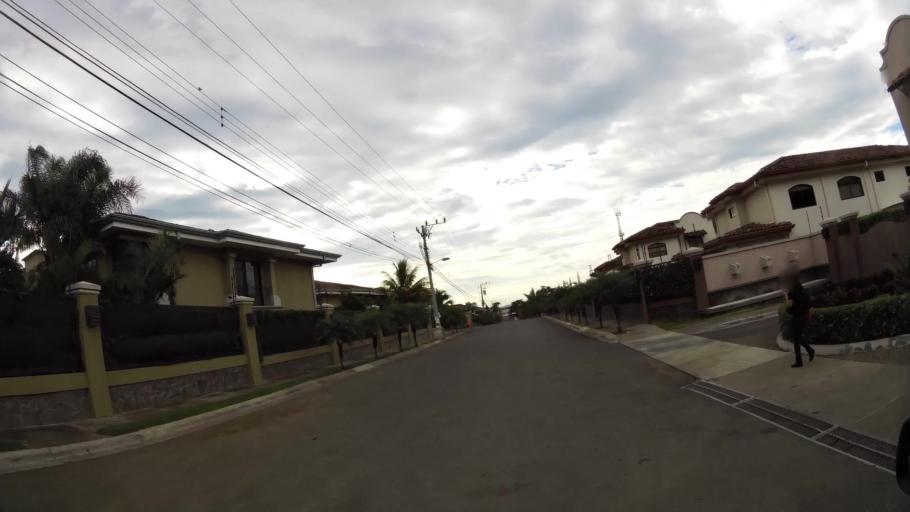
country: CR
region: San Jose
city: Santa Ana
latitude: 9.9524
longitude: -84.1864
